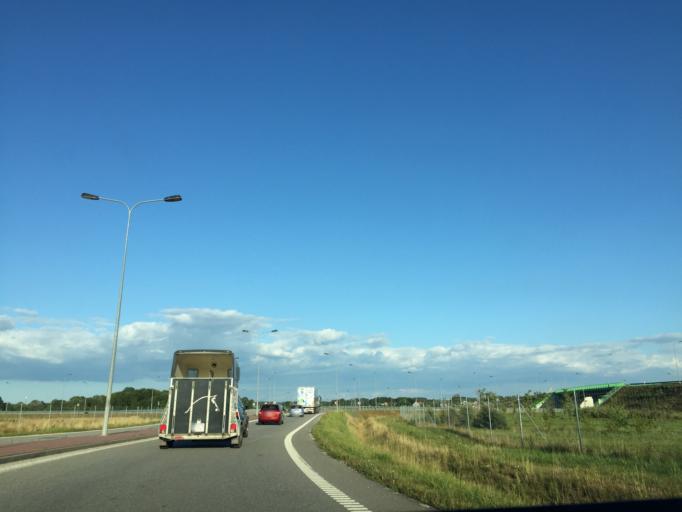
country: PL
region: Podlasie
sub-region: Powiat kolnenski
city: Stawiski
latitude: 53.3875
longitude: 22.1421
